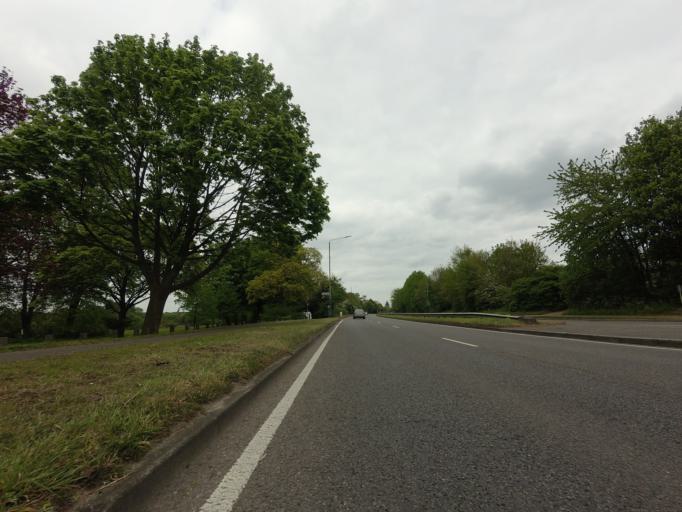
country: GB
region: England
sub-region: Greater London
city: Bexley
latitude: 51.4267
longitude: 0.1355
